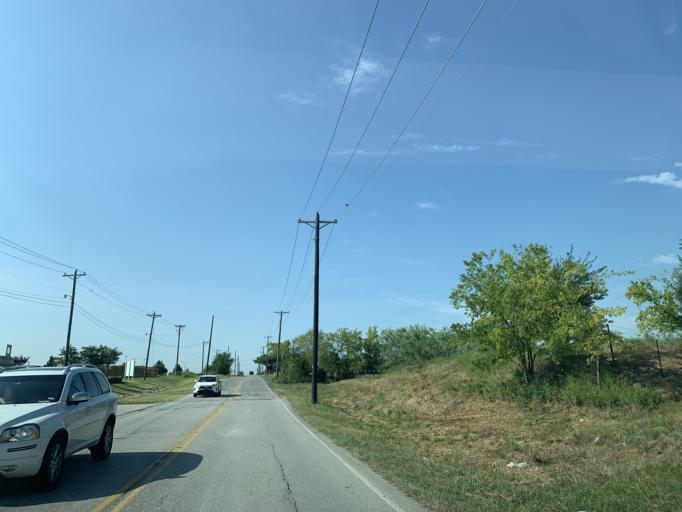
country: US
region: Texas
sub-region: Tarrant County
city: Blue Mound
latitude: 32.9013
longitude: -97.3070
